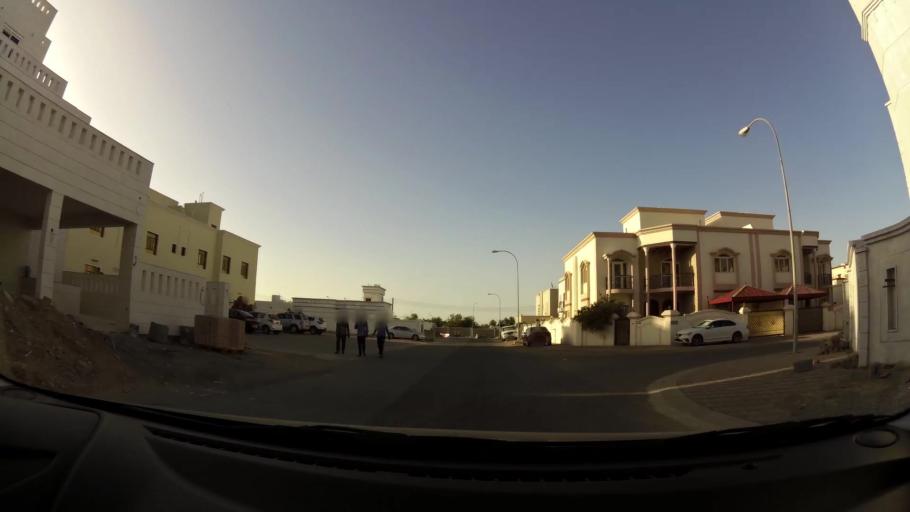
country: OM
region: Muhafazat Masqat
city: As Sib al Jadidah
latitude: 23.6105
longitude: 58.2326
